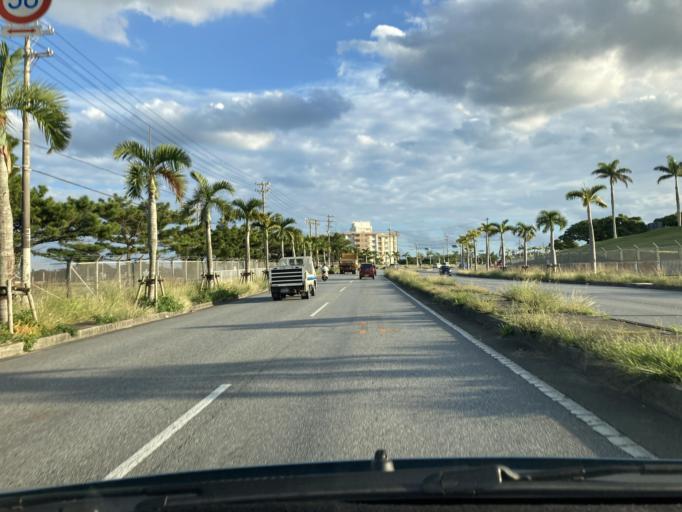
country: JP
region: Okinawa
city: Chatan
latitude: 26.3027
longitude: 127.7798
